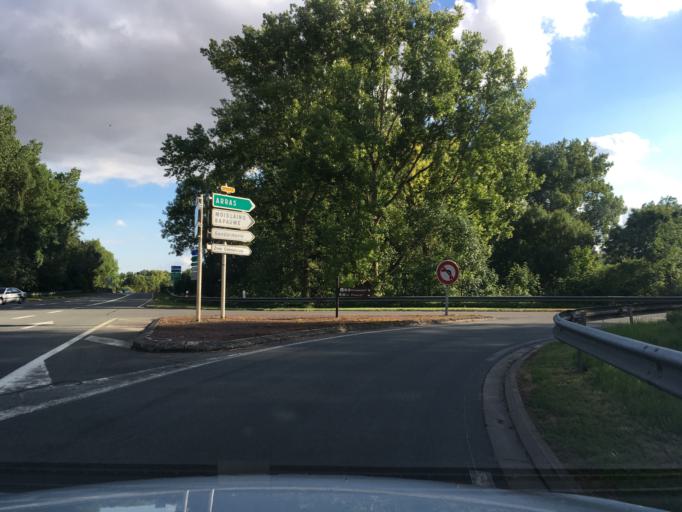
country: FR
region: Picardie
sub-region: Departement de la Somme
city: Peronne
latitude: 49.9375
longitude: 2.9485
